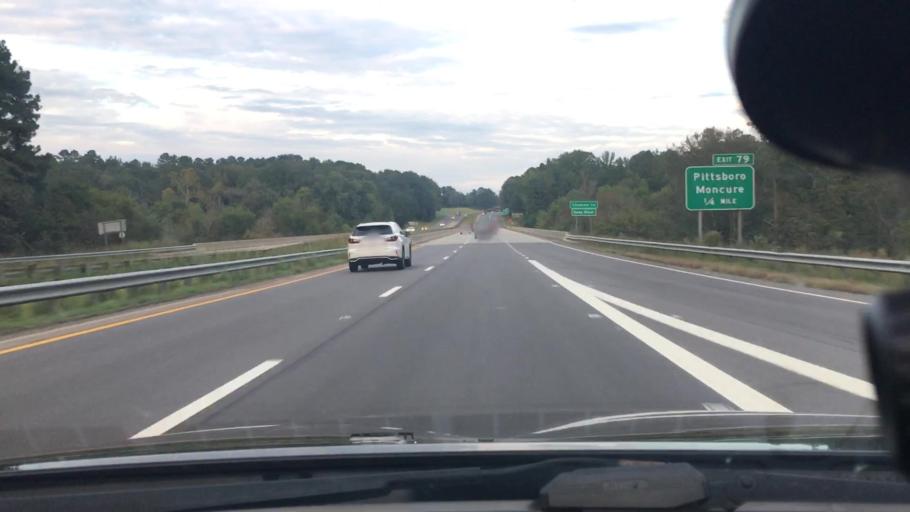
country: US
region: North Carolina
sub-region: Chatham County
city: Pittsboro
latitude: 35.6184
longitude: -79.0953
